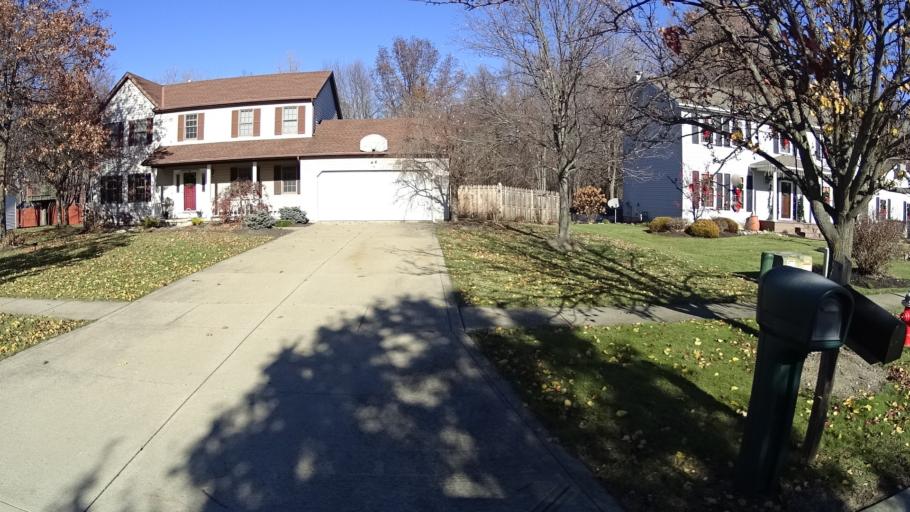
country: US
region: Ohio
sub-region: Lorain County
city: Avon Center
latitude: 41.4302
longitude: -82.0012
